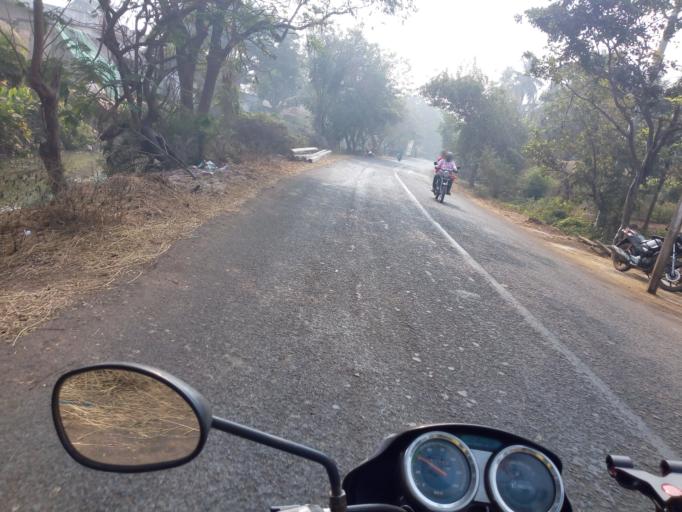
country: IN
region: Andhra Pradesh
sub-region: West Godavari
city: Tadepallegudem
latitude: 16.7788
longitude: 81.4213
